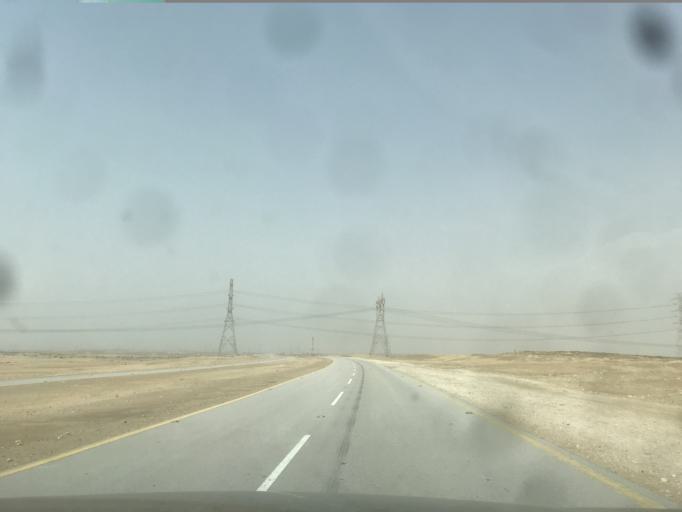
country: SA
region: Eastern Province
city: Abqaiq
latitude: 25.9272
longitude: 49.7569
